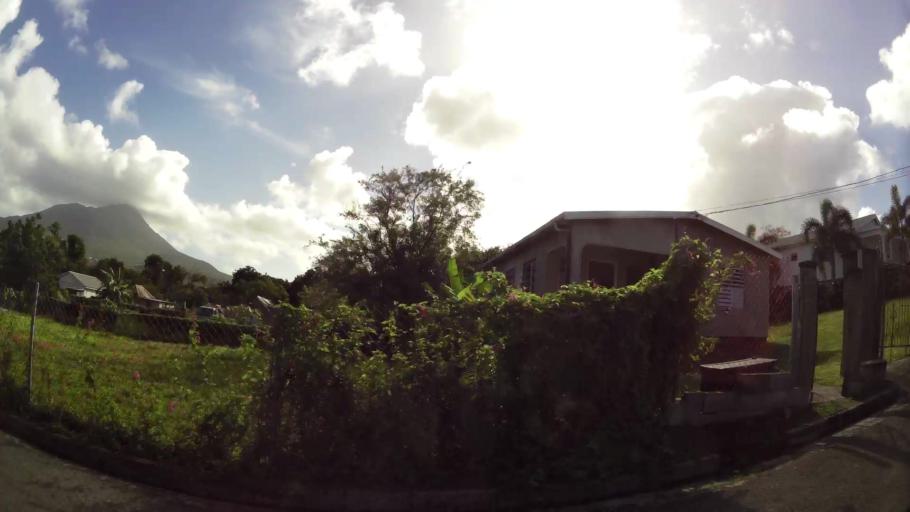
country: KN
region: Saint Paul Charlestown
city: Charlestown
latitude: 17.1323
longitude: -62.6292
